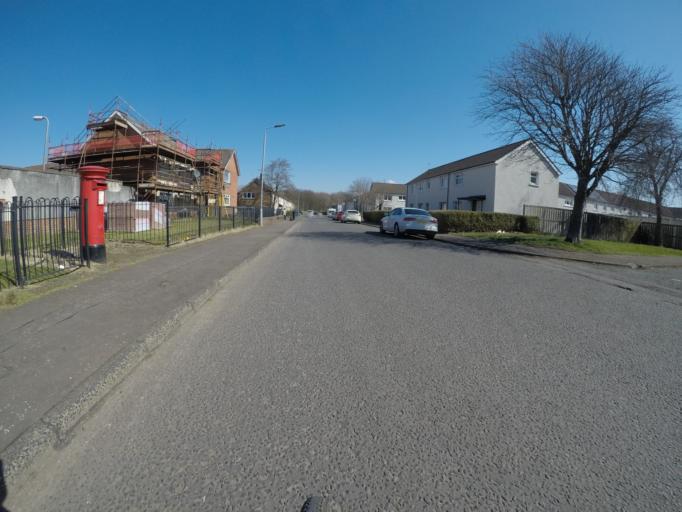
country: GB
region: Scotland
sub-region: North Ayrshire
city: Irvine
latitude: 55.6272
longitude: -4.6594
